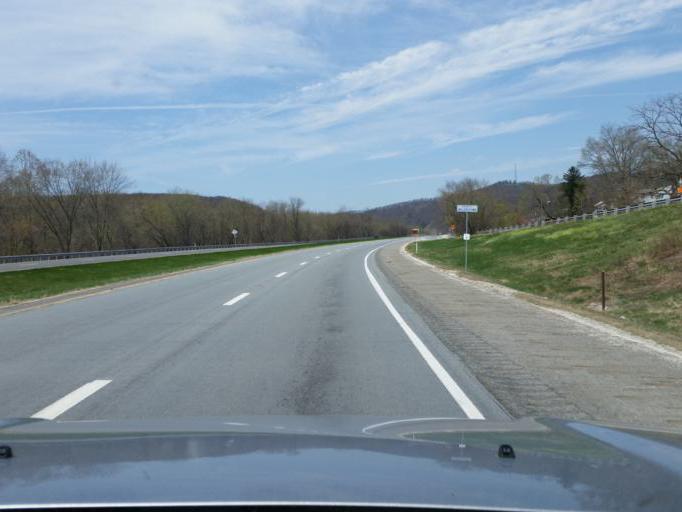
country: US
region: Pennsylvania
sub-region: Perry County
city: Newport
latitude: 40.5451
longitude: -77.1530
